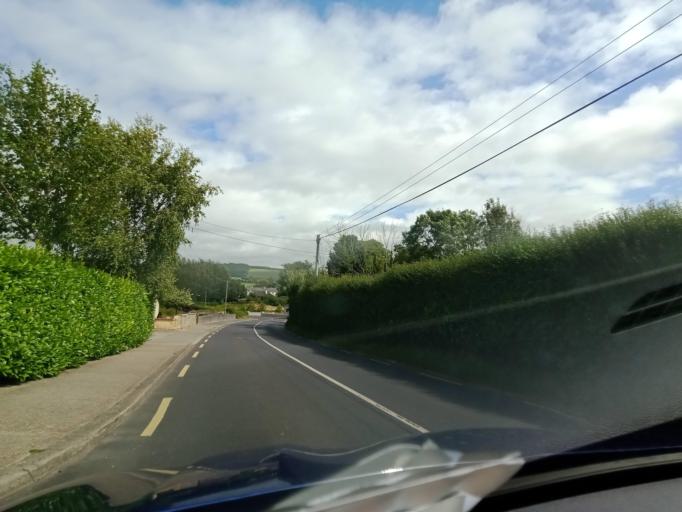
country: IE
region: Leinster
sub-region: Laois
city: Abbeyleix
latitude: 52.9469
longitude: -7.3083
